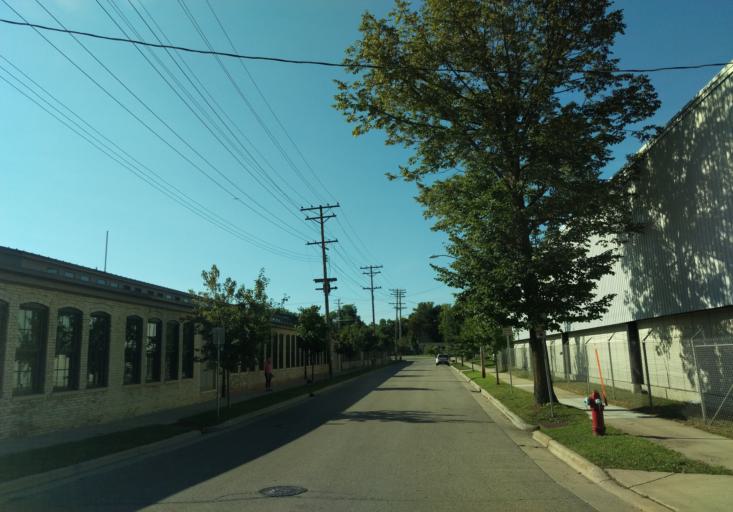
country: US
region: Wisconsin
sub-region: Dane County
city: Monona
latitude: 43.0977
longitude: -89.3440
